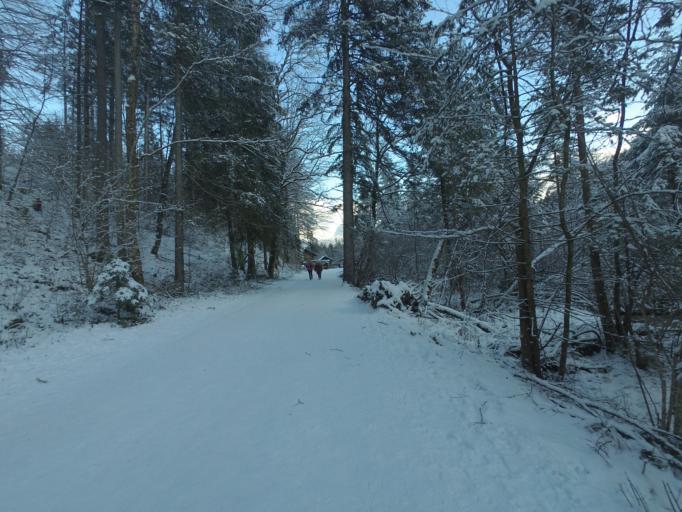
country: AT
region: Salzburg
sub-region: Politischer Bezirk Hallein
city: Golling an der Salzach
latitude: 47.5831
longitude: 13.1466
